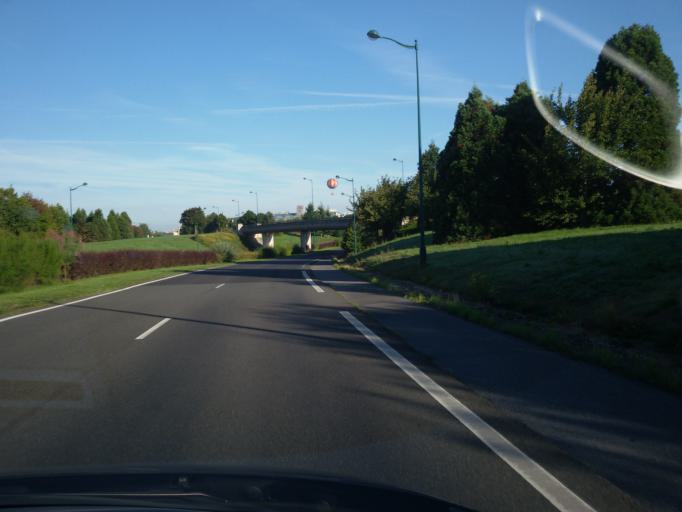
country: FR
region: Ile-de-France
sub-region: Departement de Seine-et-Marne
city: Serris
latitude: 48.8583
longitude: 2.7957
